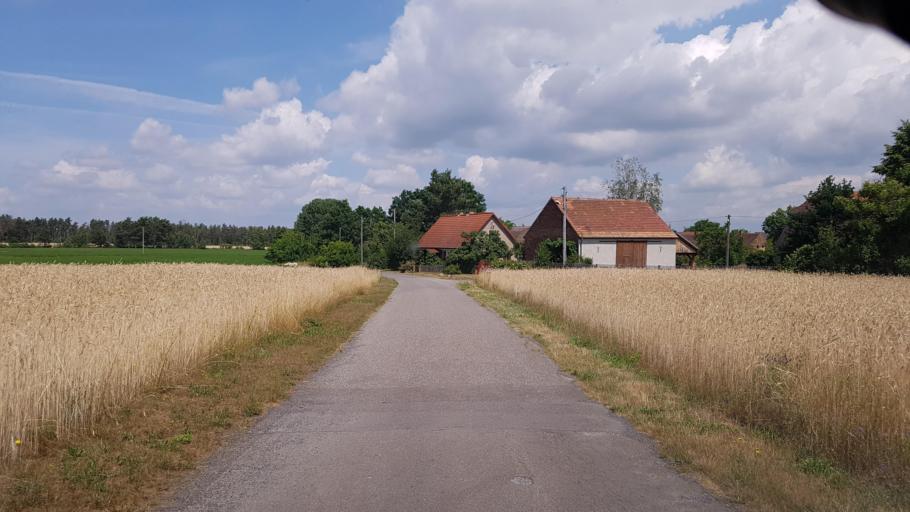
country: DE
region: Brandenburg
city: Crinitz
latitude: 51.7465
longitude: 13.8299
